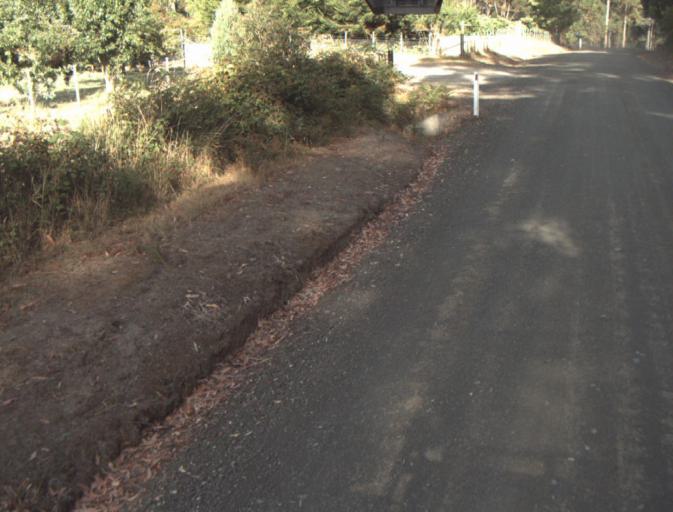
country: AU
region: Tasmania
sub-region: Launceston
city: Mayfield
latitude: -41.2709
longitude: 147.1739
